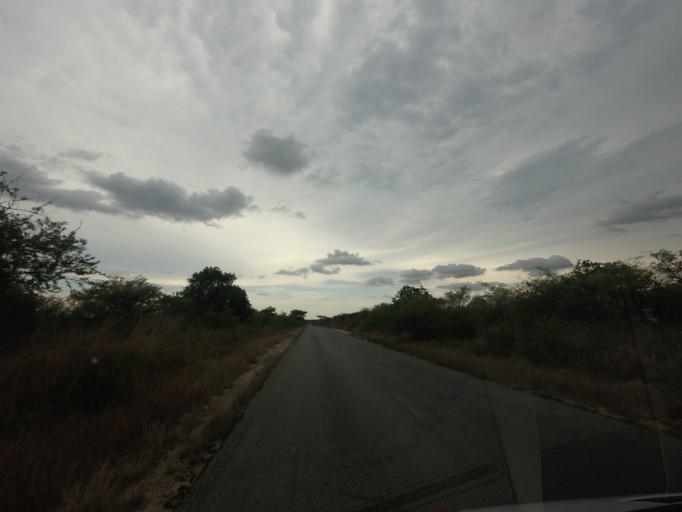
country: ZA
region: Limpopo
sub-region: Mopani District Municipality
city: Hoedspruit
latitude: -24.5286
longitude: 30.9789
